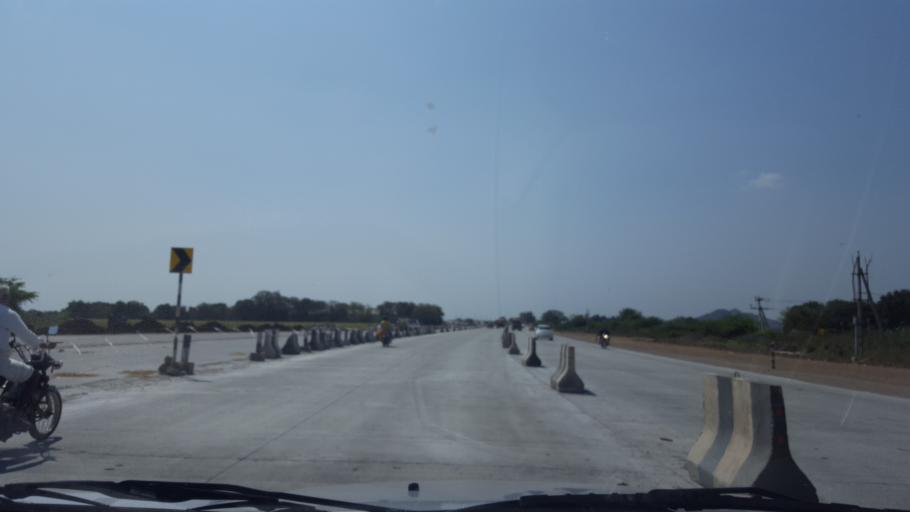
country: IN
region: Andhra Pradesh
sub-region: Prakasam
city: Addanki
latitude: 15.7642
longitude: 80.0330
